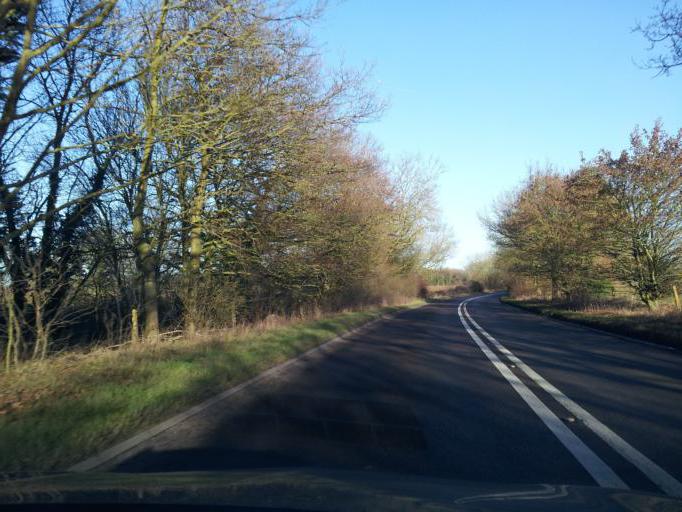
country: GB
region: England
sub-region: Suffolk
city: Lavenham
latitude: 52.1355
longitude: 0.7544
